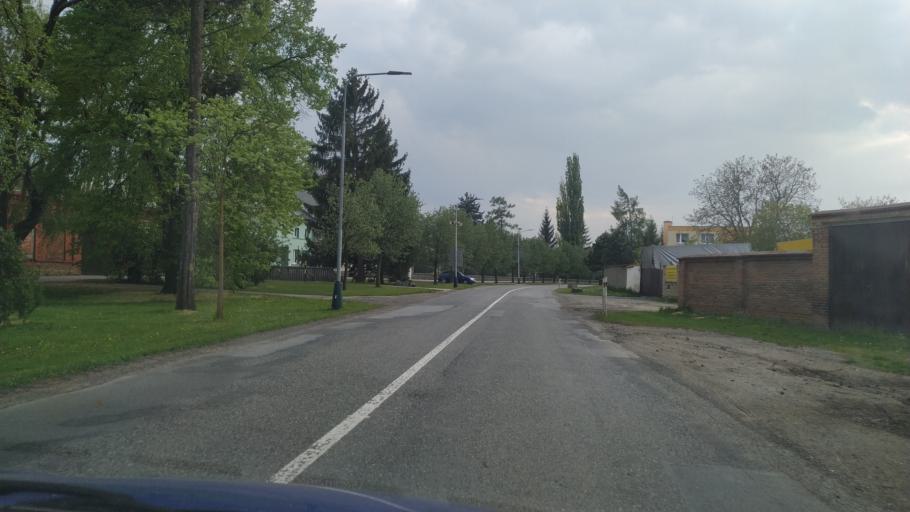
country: CZ
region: Olomoucky
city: Lutin
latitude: 49.5590
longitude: 17.1394
